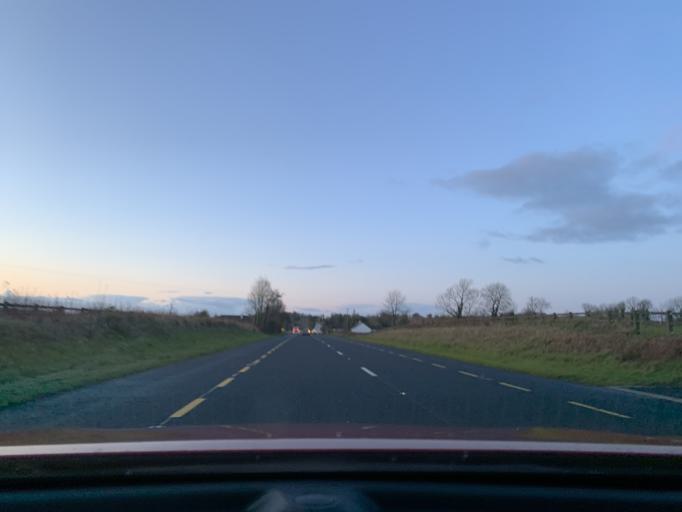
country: IE
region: Connaught
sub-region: County Leitrim
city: Carrick-on-Shannon
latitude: 53.9101
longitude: -7.9655
